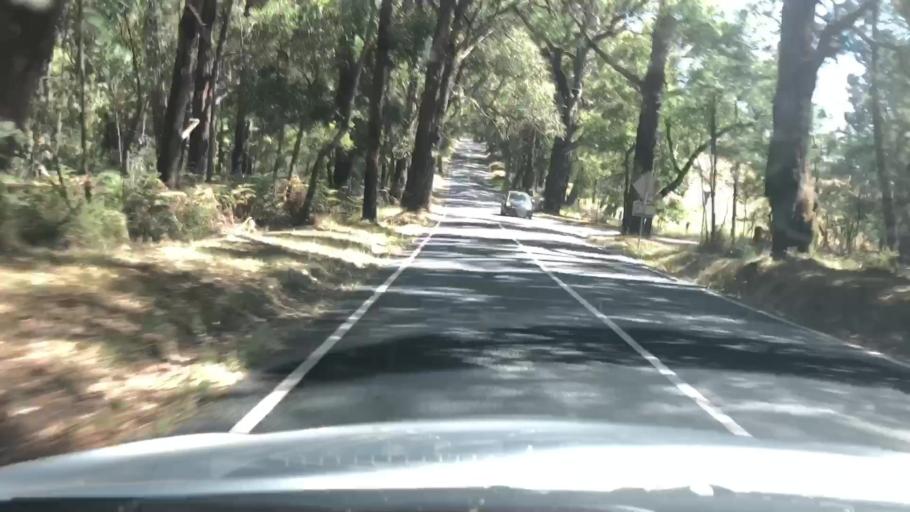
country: AU
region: Victoria
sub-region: Yarra Ranges
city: Macclesfield
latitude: -37.8569
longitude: 145.4815
